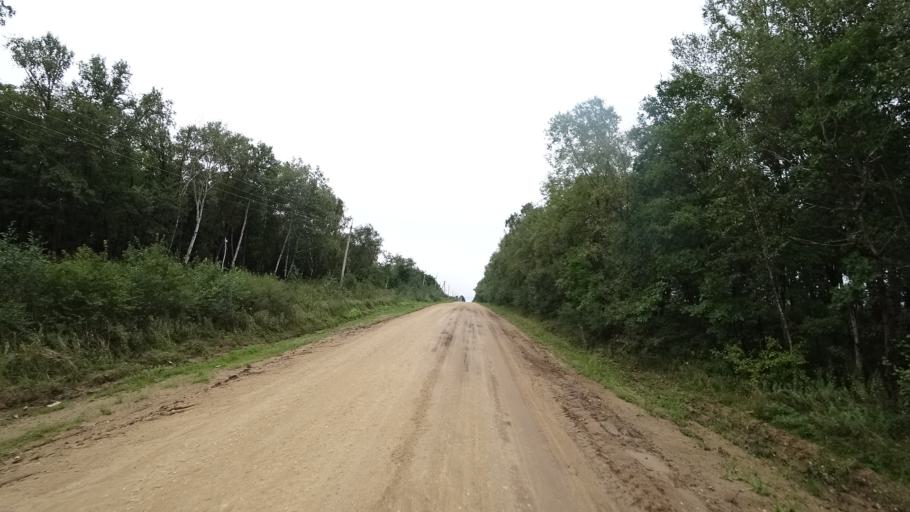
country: RU
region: Primorskiy
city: Ivanovka
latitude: 44.0741
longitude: 132.5846
